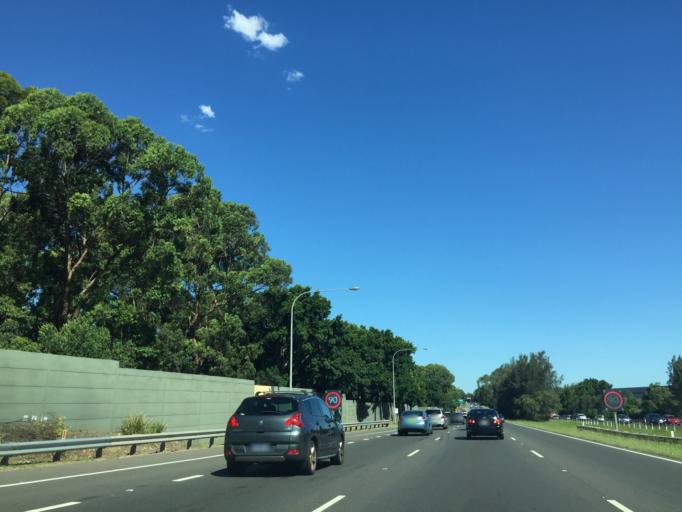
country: AU
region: New South Wales
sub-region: Auburn
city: Auburn
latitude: -33.8454
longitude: 151.0483
